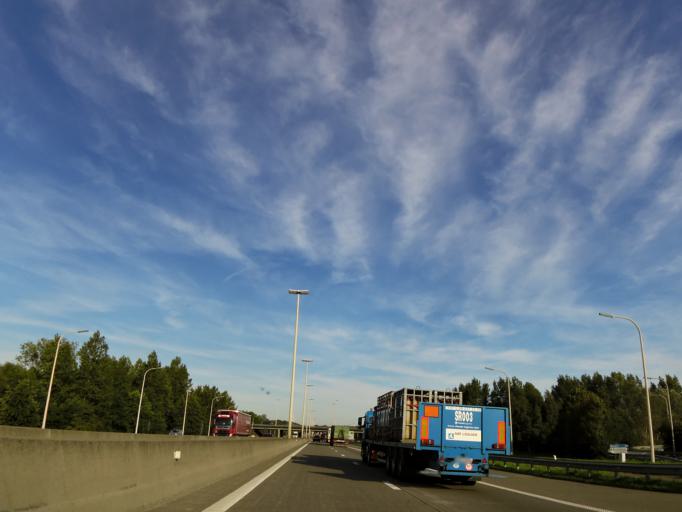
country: BE
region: Flanders
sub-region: Provincie Limburg
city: Tessenderlo
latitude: 51.0759
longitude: 5.1403
